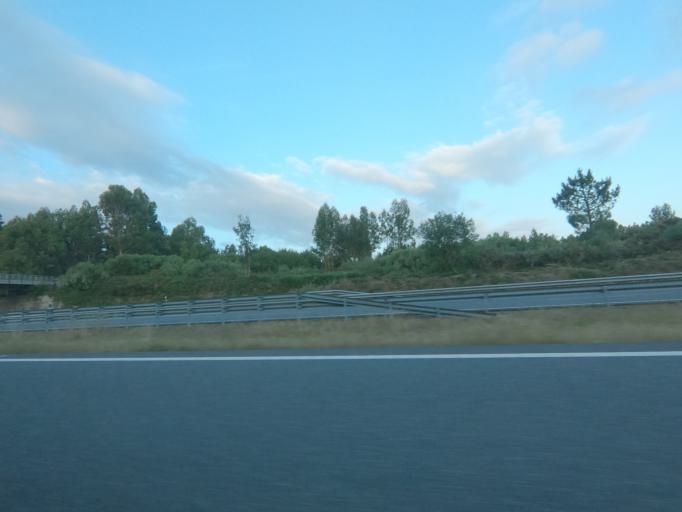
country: ES
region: Galicia
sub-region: Provincia de Ourense
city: Melon
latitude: 42.2146
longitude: -8.2595
